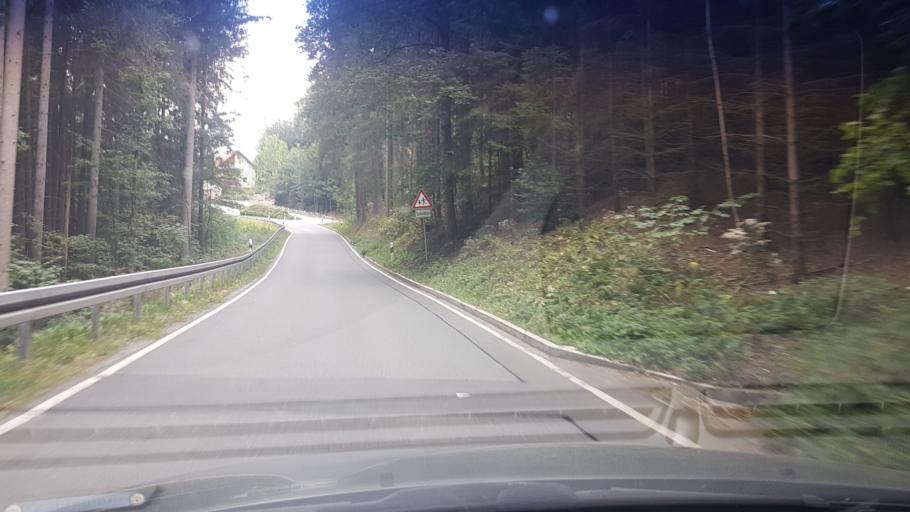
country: DE
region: Bavaria
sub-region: Upper Franconia
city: Bad Berneck im Fichtelgebirge
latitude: 50.0686
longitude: 11.6712
